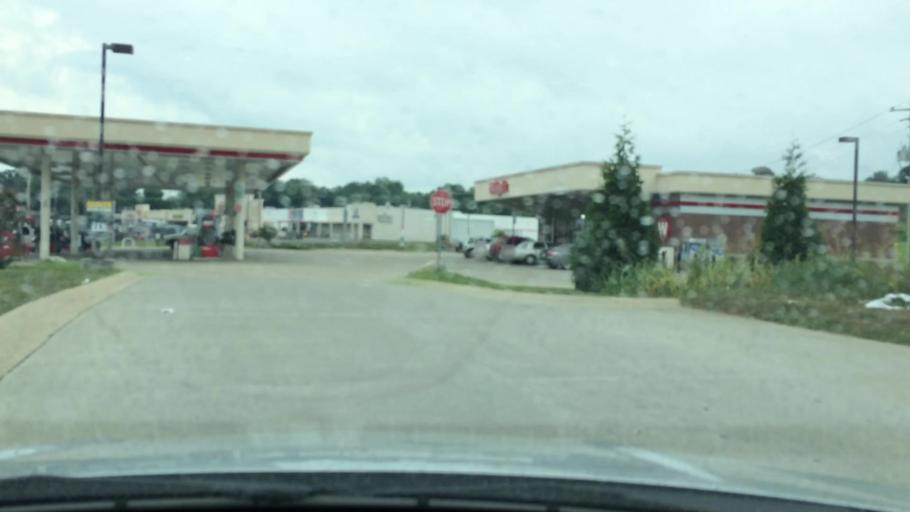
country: US
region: Tennessee
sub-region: Jefferson County
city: Jefferson City
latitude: 36.1139
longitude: -83.4972
